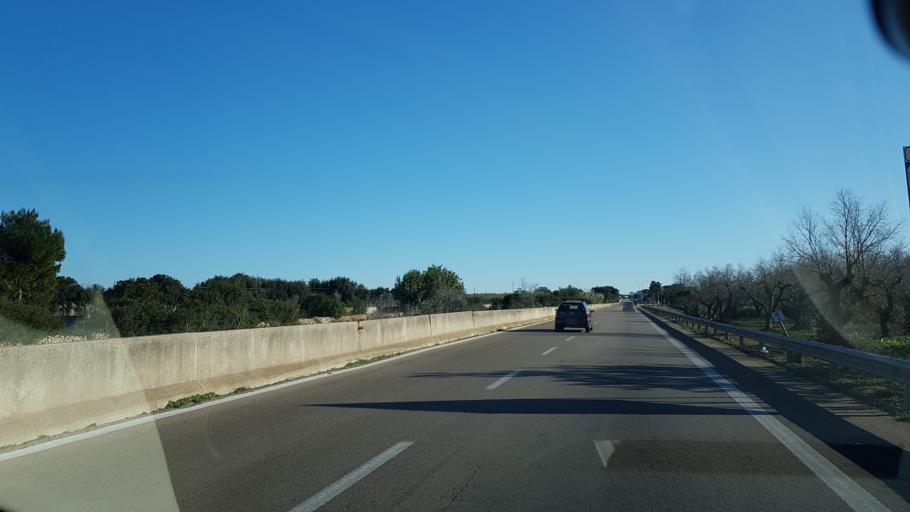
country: IT
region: Apulia
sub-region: Provincia di Lecce
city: Alezio
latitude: 40.0199
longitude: 18.0425
